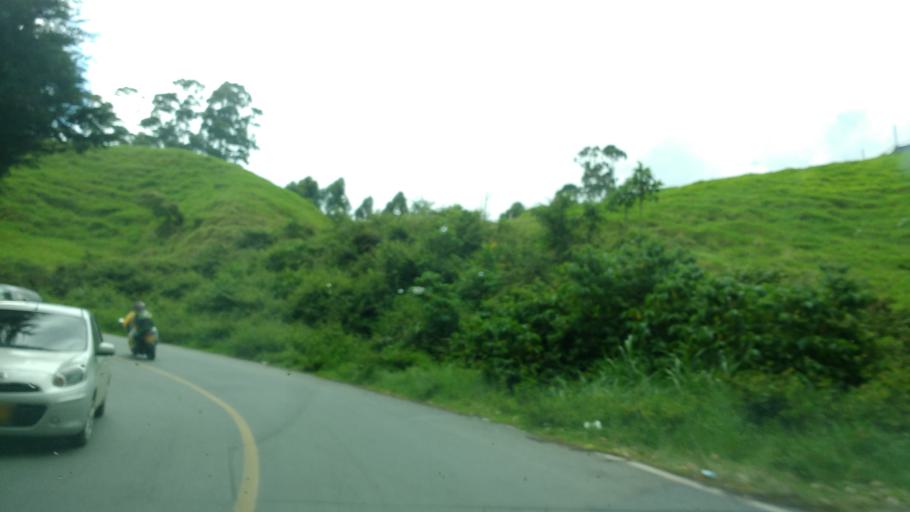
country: CO
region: Antioquia
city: Marinilla
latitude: 6.2000
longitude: -75.2850
